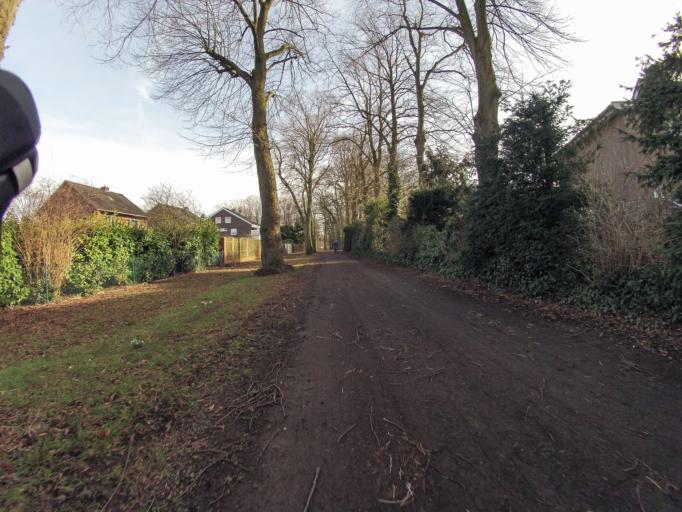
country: DE
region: North Rhine-Westphalia
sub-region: Regierungsbezirk Munster
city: Rheine
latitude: 52.2660
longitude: 7.4510
